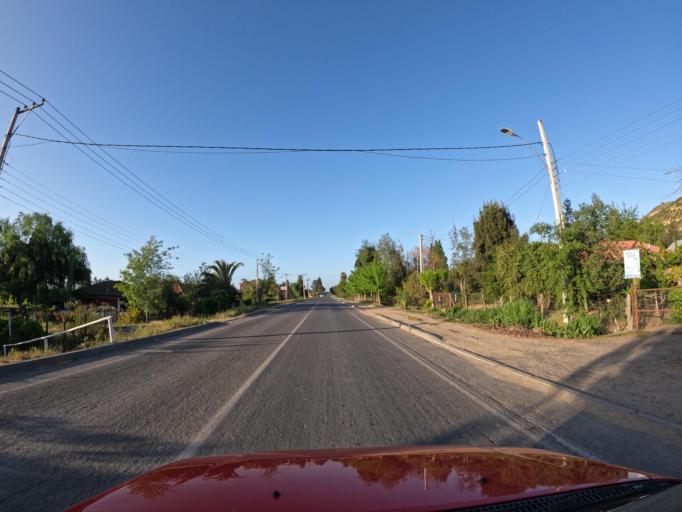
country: CL
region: O'Higgins
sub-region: Provincia de Colchagua
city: Santa Cruz
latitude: -34.3484
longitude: -71.4073
